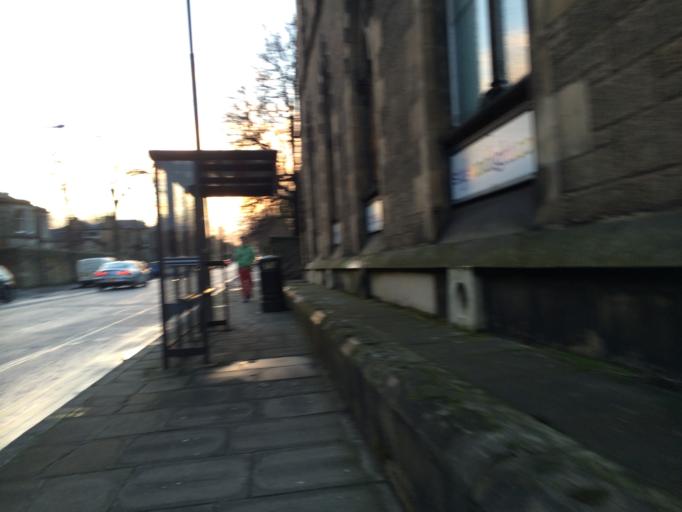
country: GB
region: Scotland
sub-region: Edinburgh
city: Edinburgh
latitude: 55.9369
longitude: -3.1809
